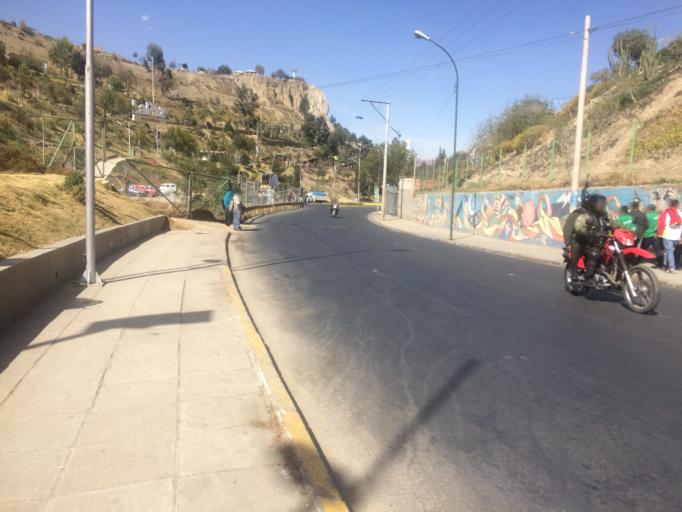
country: BO
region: La Paz
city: La Paz
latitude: -16.5033
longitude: -68.1271
